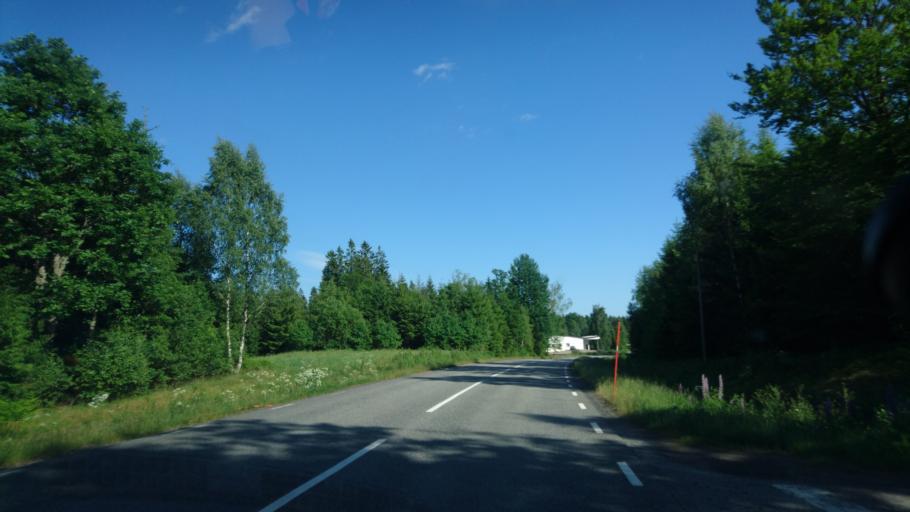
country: SE
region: Skane
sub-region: Osby Kommun
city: Lonsboda
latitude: 56.4239
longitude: 14.2815
